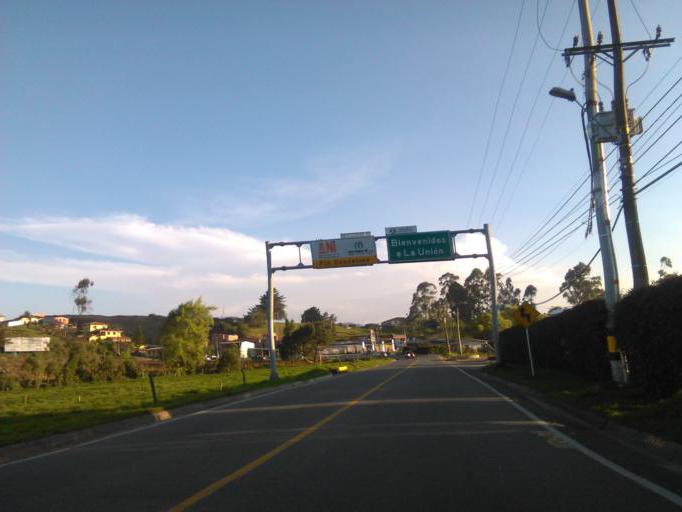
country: CO
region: Antioquia
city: La Union
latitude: 5.9842
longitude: -75.3719
